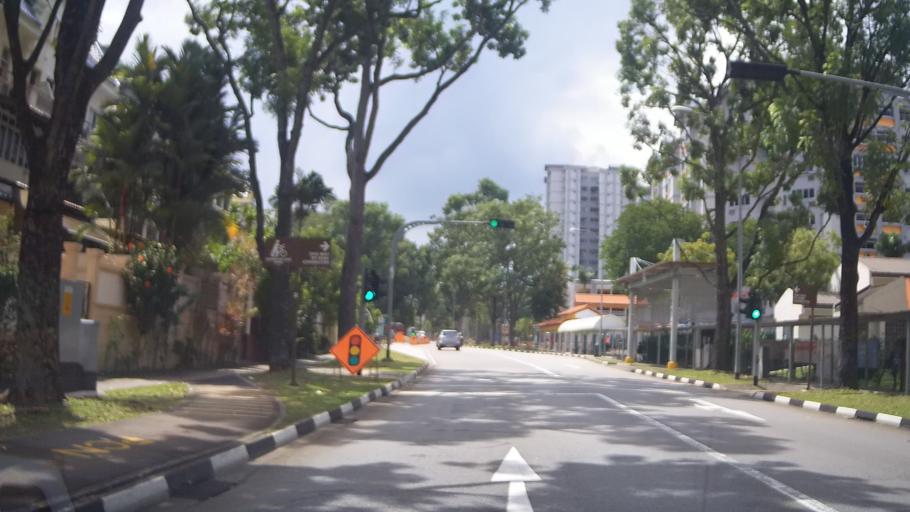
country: MY
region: Johor
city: Johor Bahru
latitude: 1.3926
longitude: 103.7507
